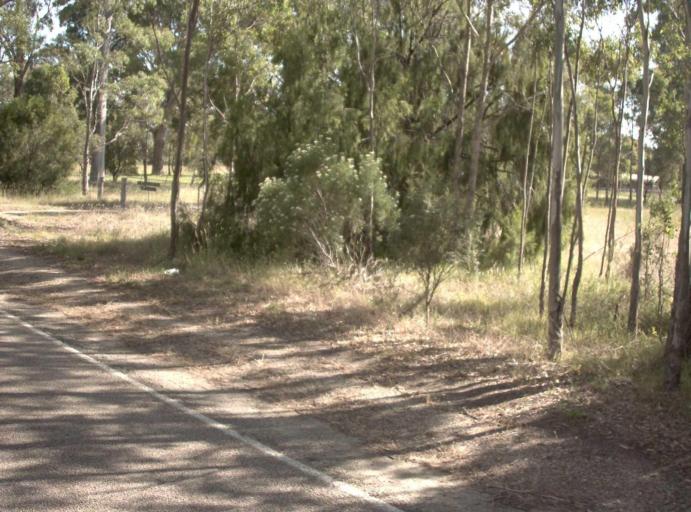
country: AU
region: Victoria
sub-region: East Gippsland
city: Lakes Entrance
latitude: -37.7945
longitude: 147.8315
